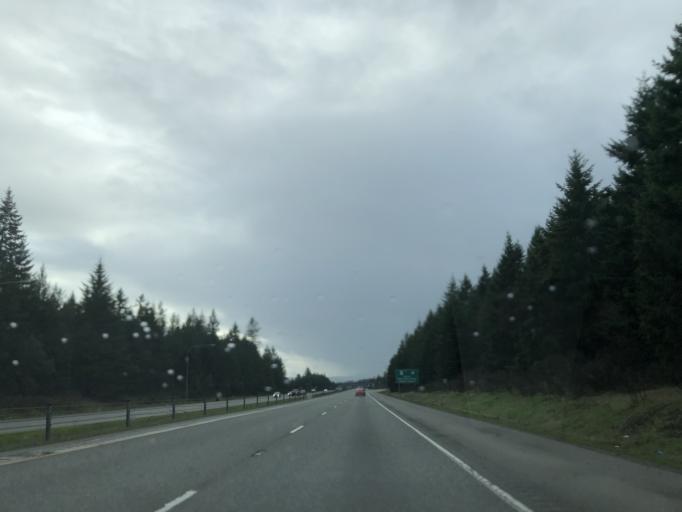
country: US
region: Washington
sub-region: Kitsap County
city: Bangor Trident Base
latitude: 47.7081
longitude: -122.6829
